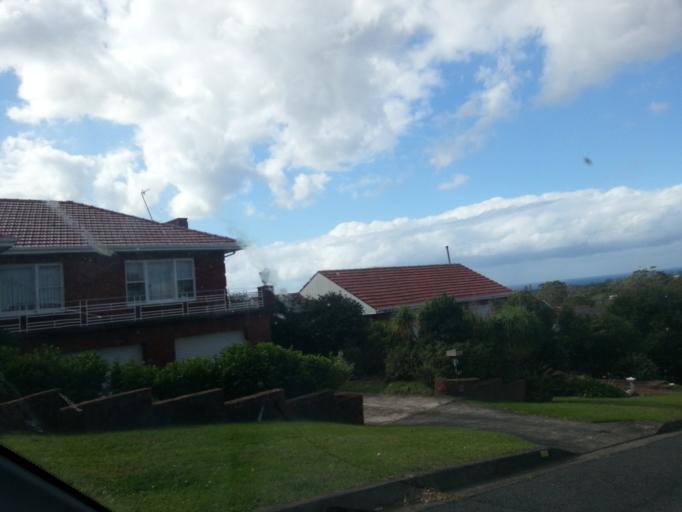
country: AU
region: New South Wales
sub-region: Wollongong
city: Keiraville
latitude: -34.4139
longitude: 150.8667
